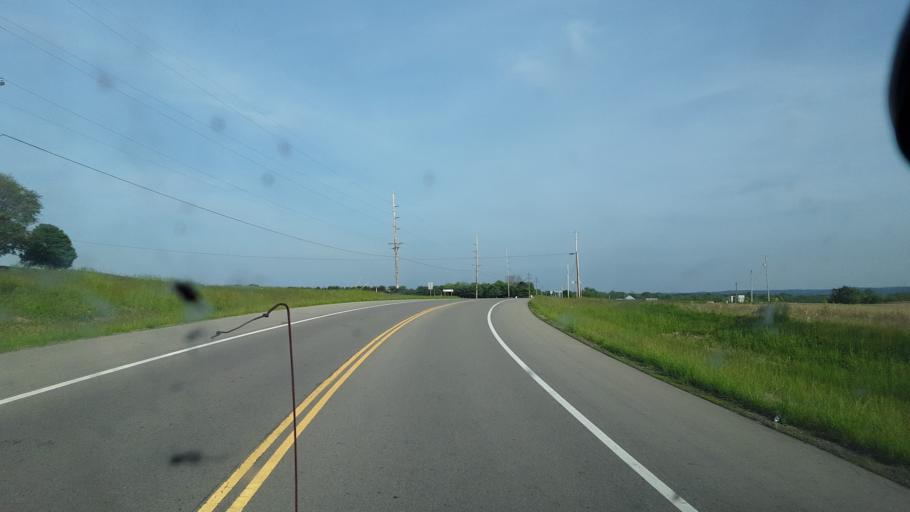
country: US
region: Ohio
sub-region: Ross County
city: Kingston
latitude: 39.5259
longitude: -82.8289
